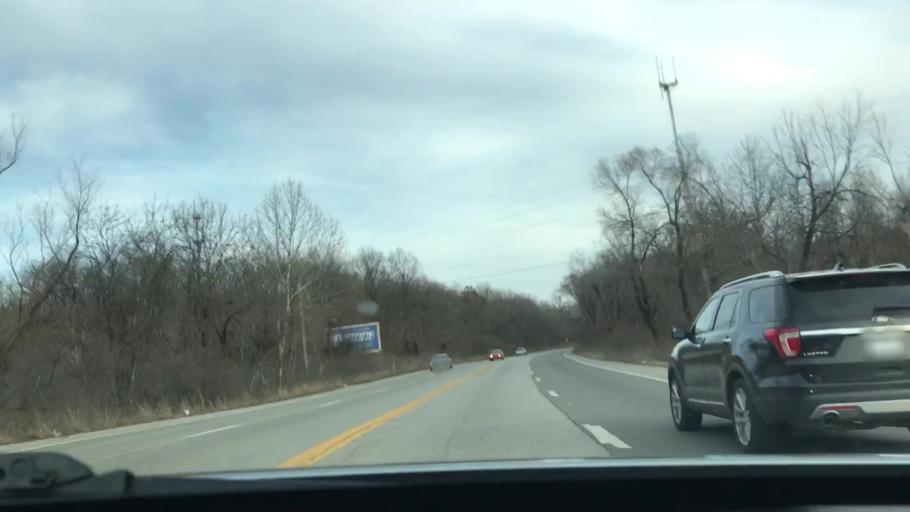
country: US
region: Missouri
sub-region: Jackson County
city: Sugar Creek
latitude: 39.0936
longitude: -94.4824
